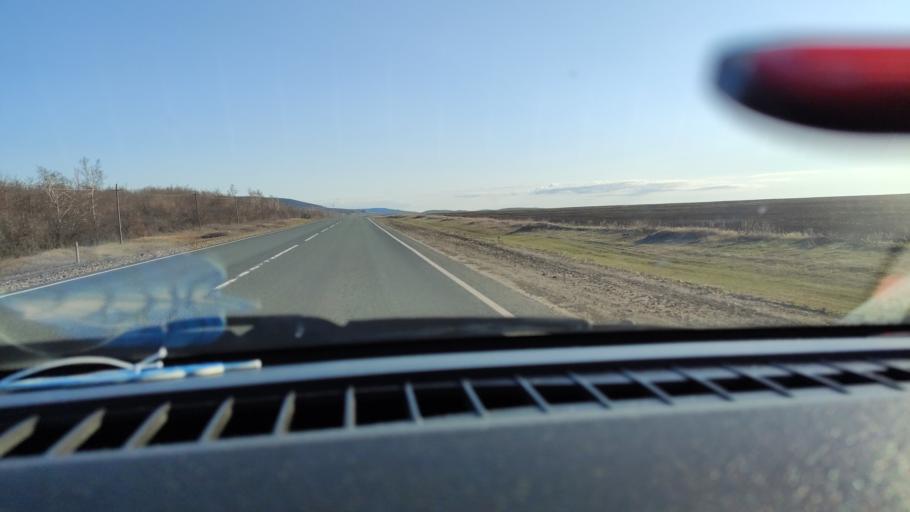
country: RU
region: Saratov
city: Alekseyevka
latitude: 52.2673
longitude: 47.9261
